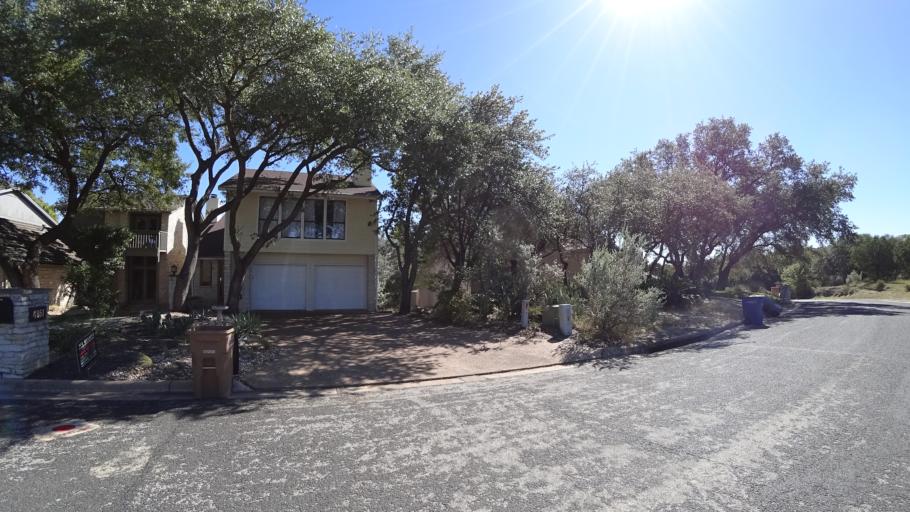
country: US
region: Texas
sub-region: Travis County
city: West Lake Hills
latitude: 30.3480
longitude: -97.7821
